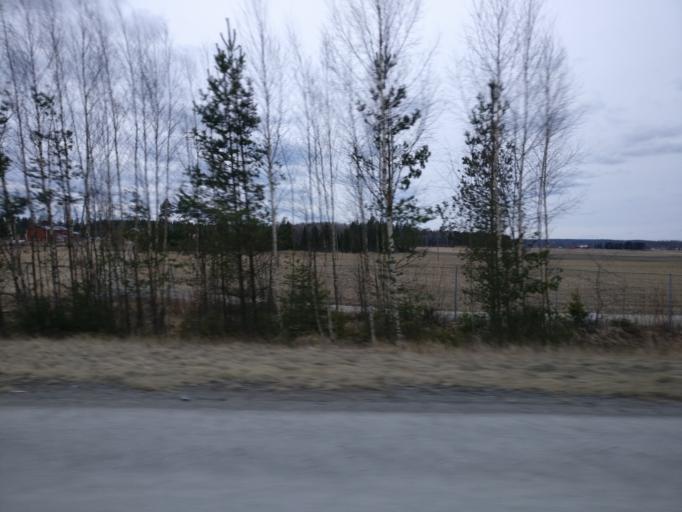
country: FI
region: Haeme
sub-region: Haemeenlinna
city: Kalvola
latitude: 61.0913
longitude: 24.1867
